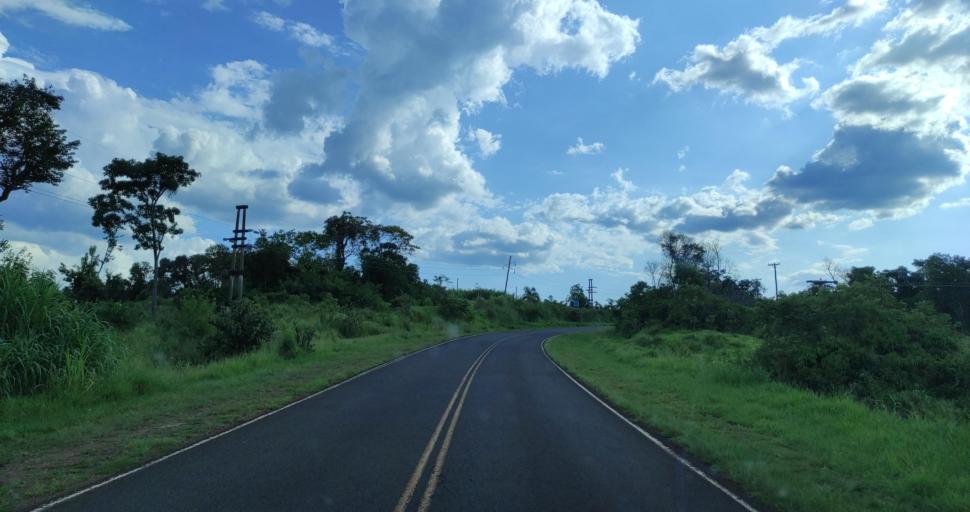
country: AR
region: Misiones
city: San Vicente
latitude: -26.3498
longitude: -54.1860
